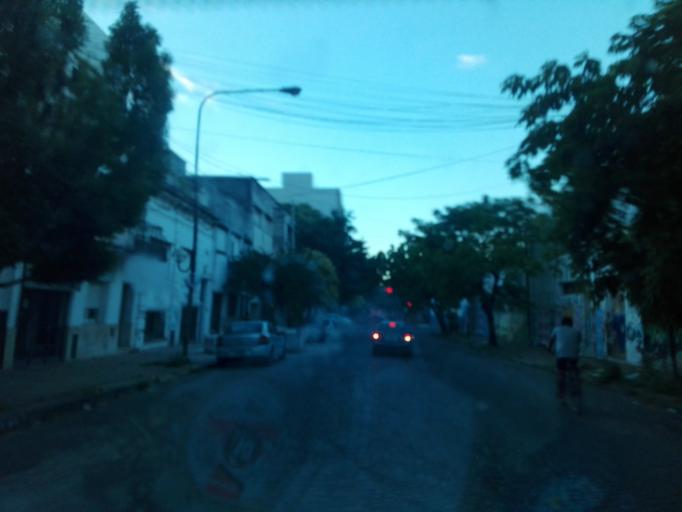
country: AR
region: Buenos Aires
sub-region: Partido de La Plata
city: La Plata
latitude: -34.9083
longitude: -57.9515
